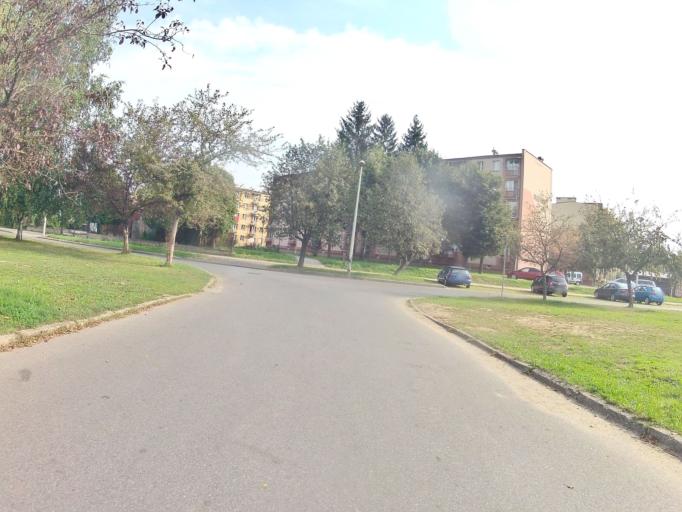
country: PL
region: Subcarpathian Voivodeship
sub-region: Powiat jasielski
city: Jaslo
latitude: 49.7439
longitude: 21.4574
